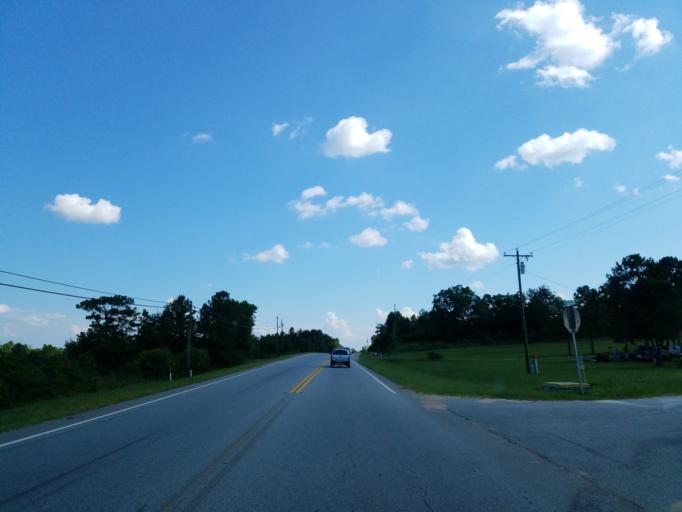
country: US
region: Georgia
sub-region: Crawford County
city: Roberta
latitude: 32.7338
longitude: -84.0163
